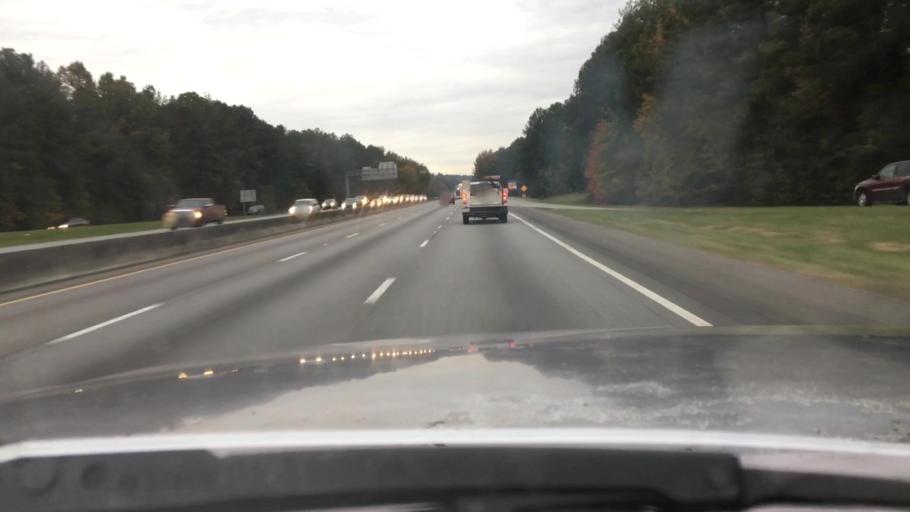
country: US
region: South Carolina
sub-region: Lexington County
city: Saint Andrews
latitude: 34.0303
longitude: -81.1232
